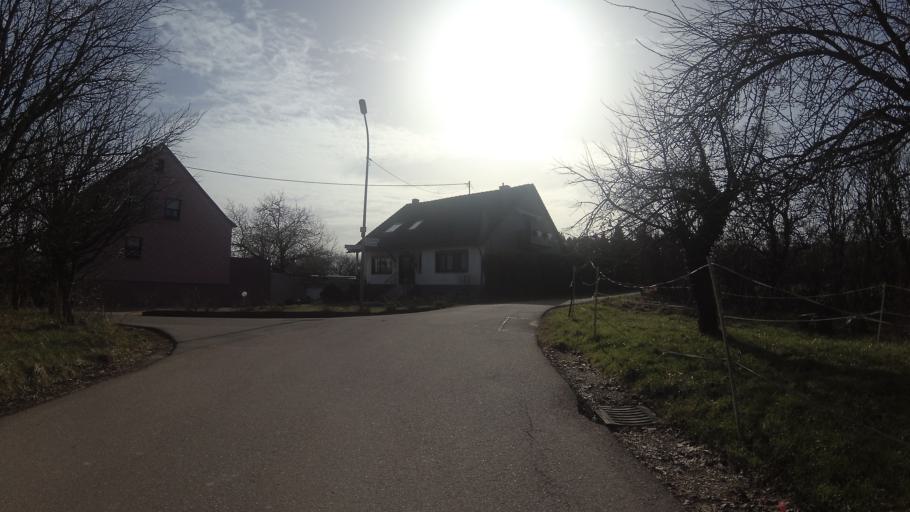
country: FR
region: Lorraine
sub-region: Departement de la Moselle
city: Merten
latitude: 49.2937
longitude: 6.6864
